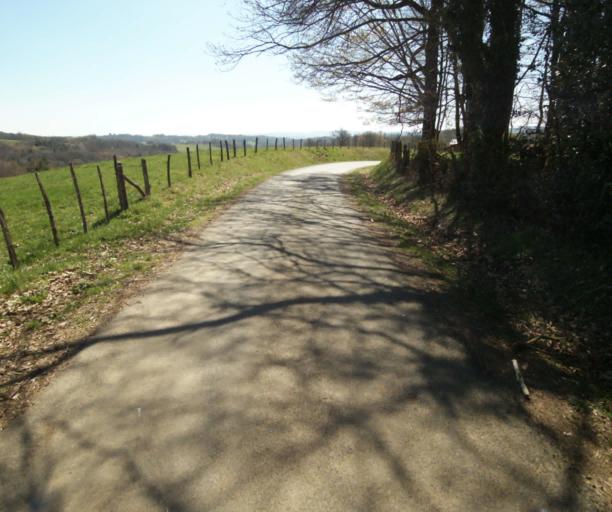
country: FR
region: Limousin
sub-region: Departement de la Correze
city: Saint-Clement
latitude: 45.3289
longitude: 1.7111
